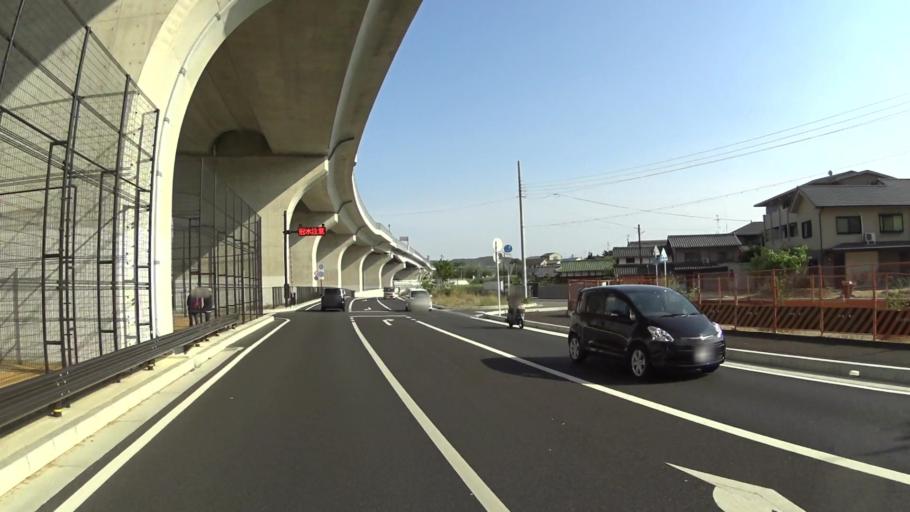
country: JP
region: Kyoto
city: Yawata
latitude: 34.9115
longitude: 135.6900
